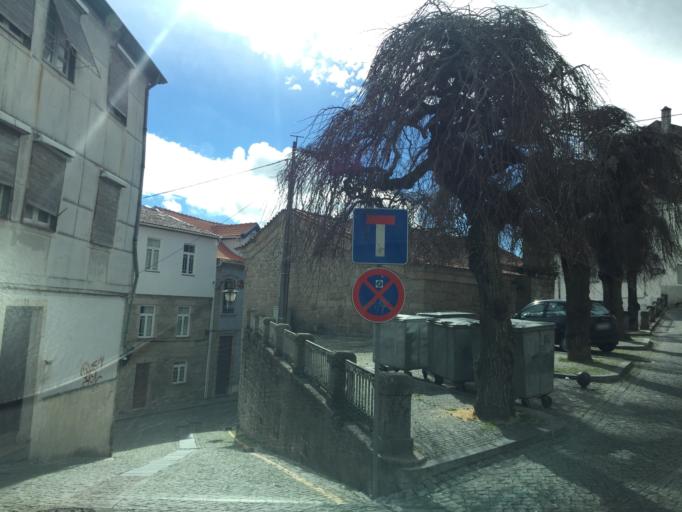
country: PT
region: Castelo Branco
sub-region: Covilha
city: Covilha
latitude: 40.2792
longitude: -7.5036
